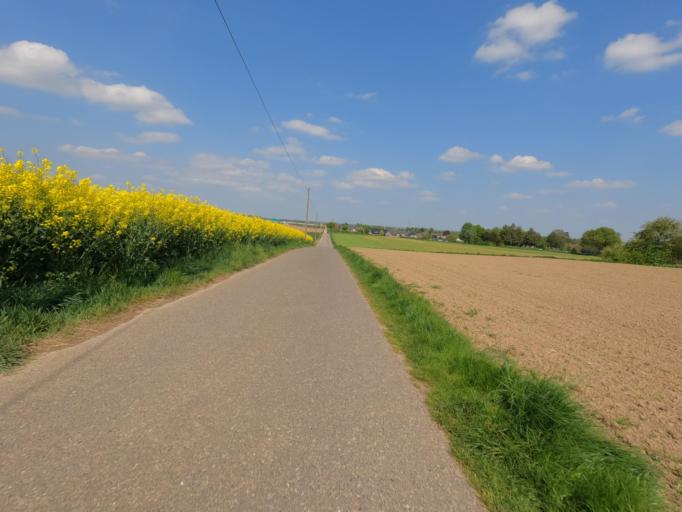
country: DE
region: North Rhine-Westphalia
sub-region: Regierungsbezirk Koln
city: Heinsberg
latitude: 51.0473
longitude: 6.0678
